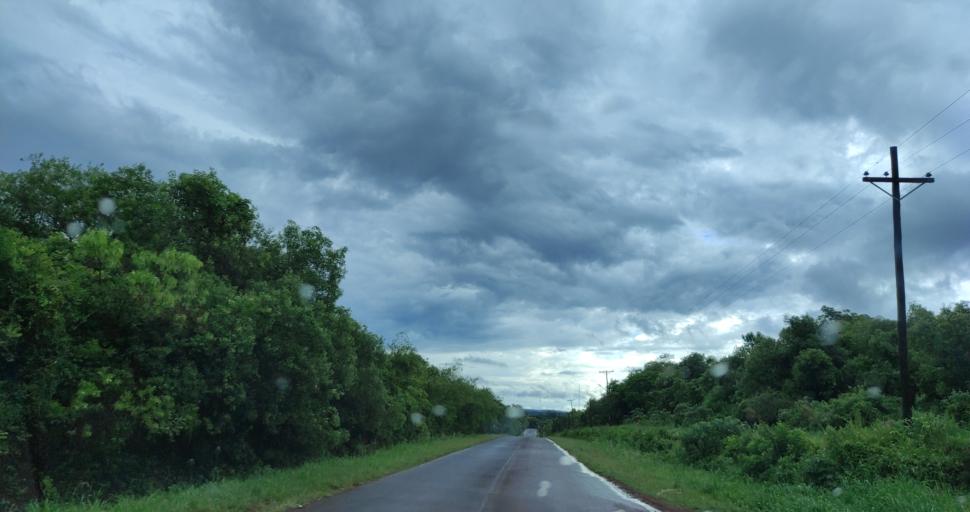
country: AR
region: Misiones
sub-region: Departamento de Apostoles
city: San Jose
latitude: -27.7721
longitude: -55.7625
